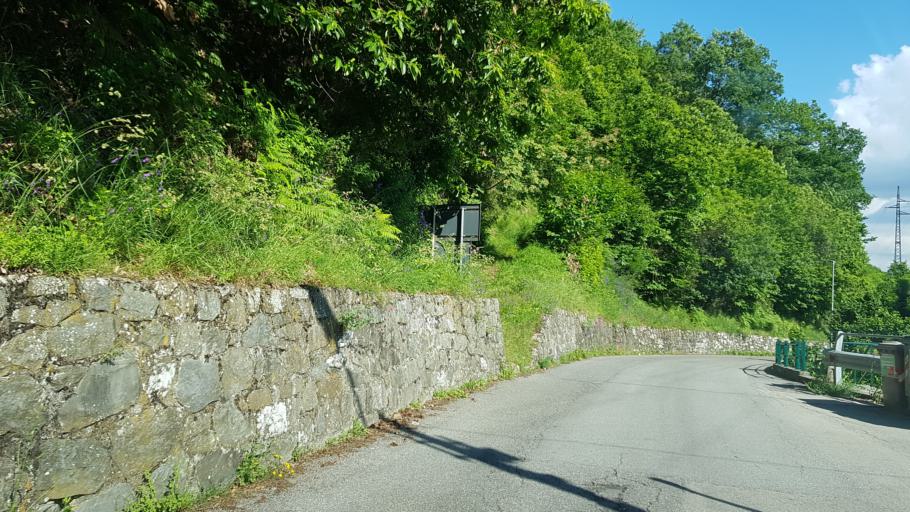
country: IT
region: Tuscany
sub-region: Provincia di Lucca
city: San Romano
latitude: 44.1795
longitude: 10.3380
